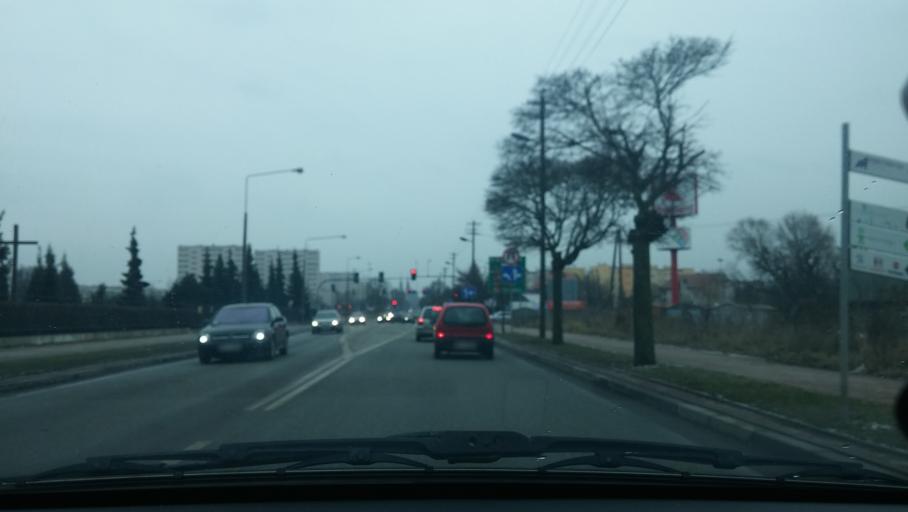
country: PL
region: Masovian Voivodeship
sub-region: Siedlce
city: Siedlce
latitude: 52.1825
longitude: 22.2690
